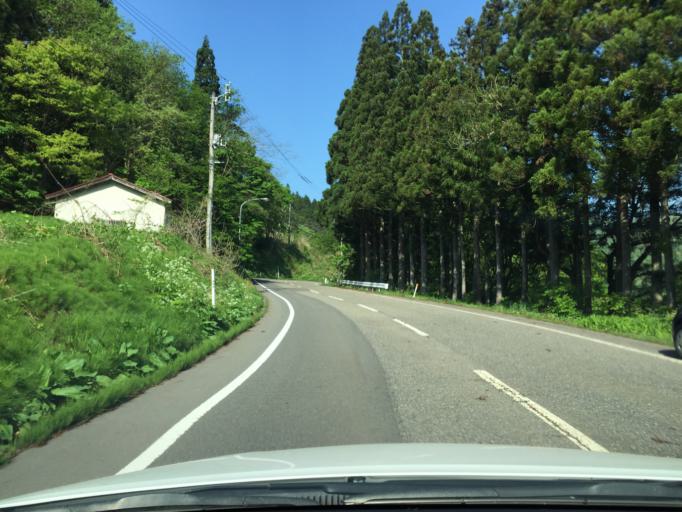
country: JP
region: Fukushima
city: Kitakata
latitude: 37.6709
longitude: 139.5841
